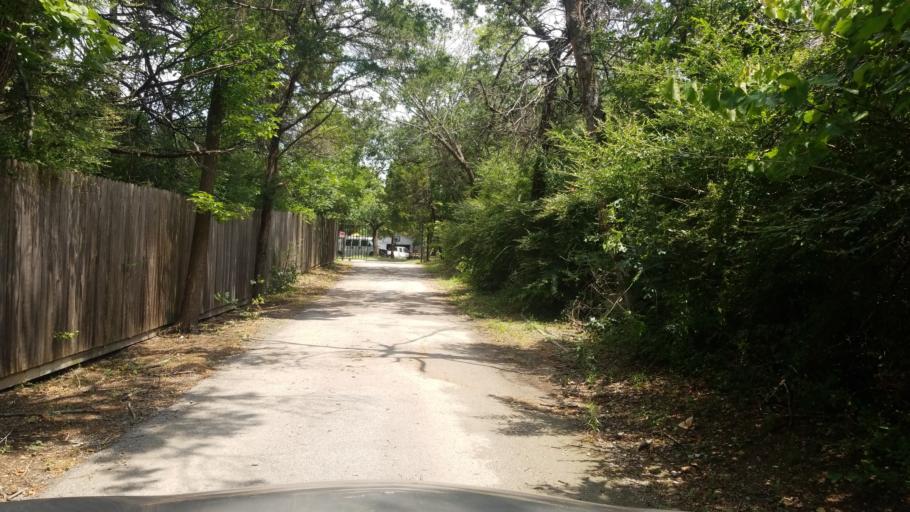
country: US
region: Texas
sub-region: Dallas County
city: Duncanville
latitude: 32.6829
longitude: -96.9245
